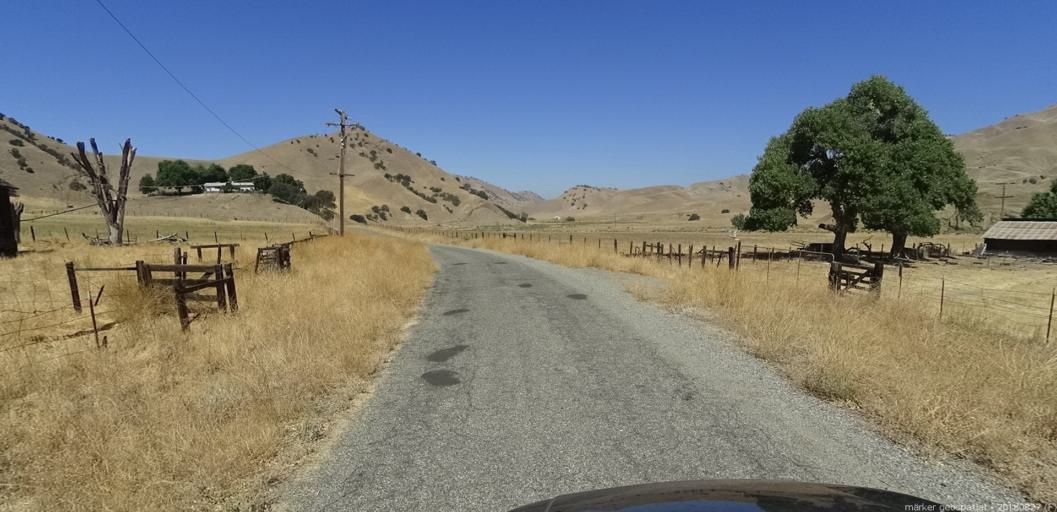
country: US
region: California
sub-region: Monterey County
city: King City
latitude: 36.3014
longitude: -120.9052
